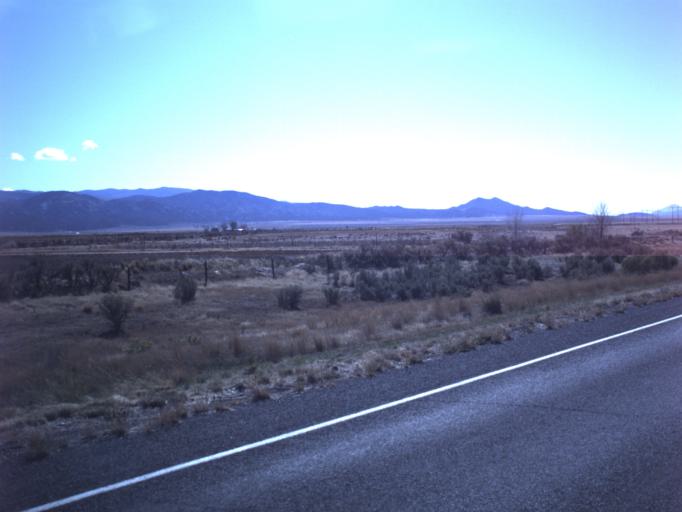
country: US
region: Utah
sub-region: Juab County
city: Nephi
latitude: 39.5367
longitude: -111.9300
